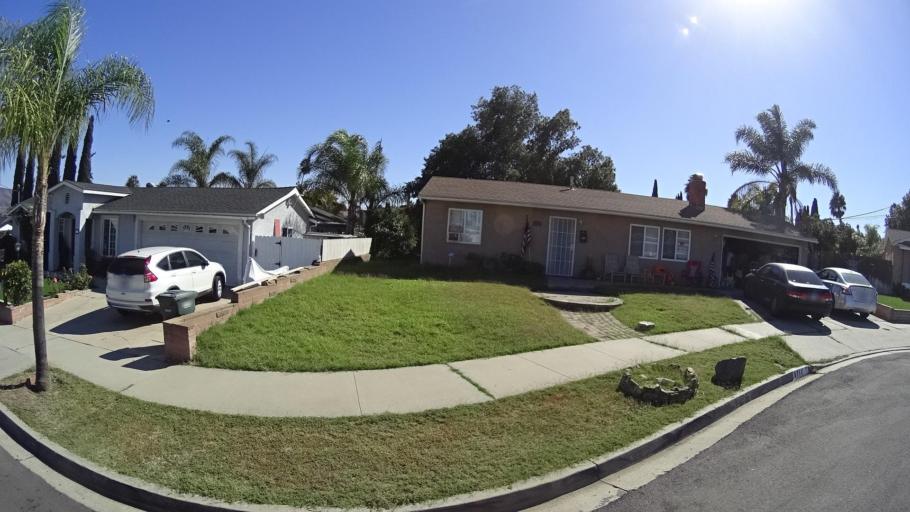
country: US
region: California
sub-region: San Diego County
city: La Presa
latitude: 32.7046
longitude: -117.0206
